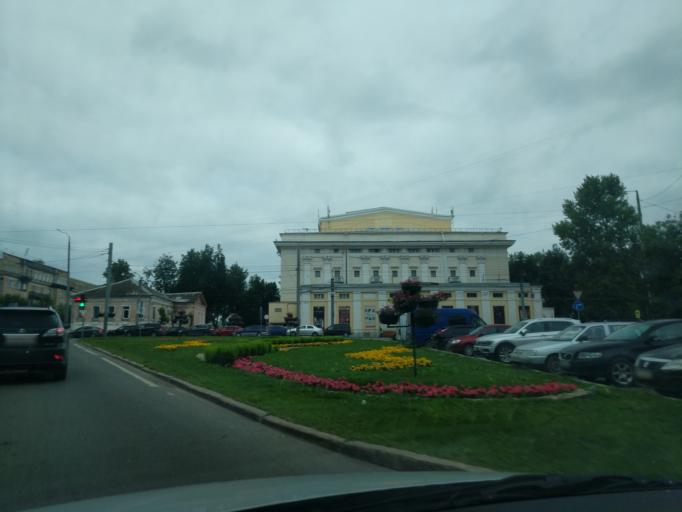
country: RU
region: Kirov
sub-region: Kirovo-Chepetskiy Rayon
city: Kirov
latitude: 58.6057
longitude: 49.6675
